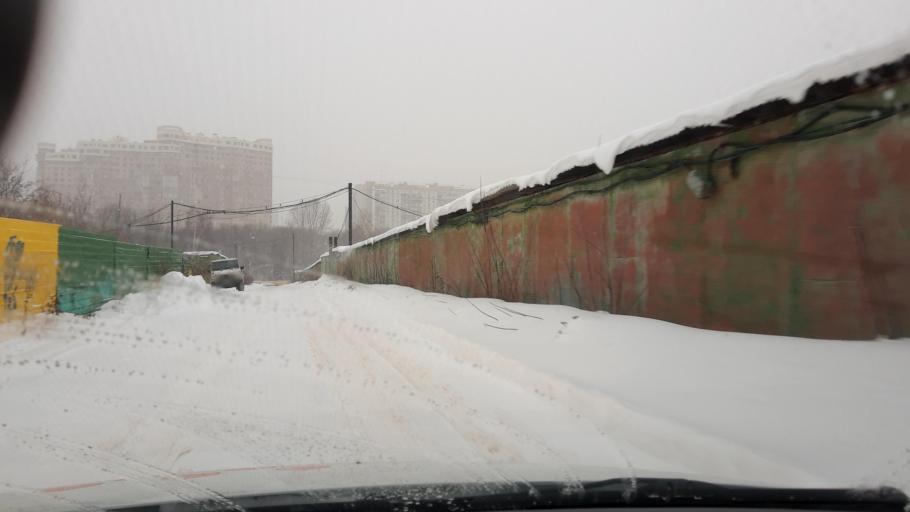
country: RU
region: Moscow
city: Ramenki
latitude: 55.6892
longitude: 37.5091
